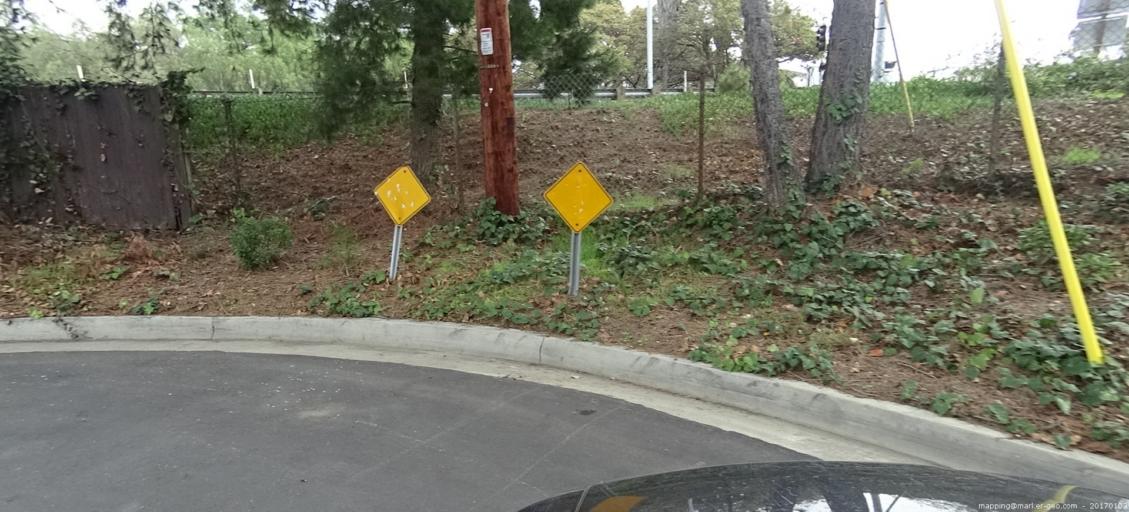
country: US
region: California
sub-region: Orange County
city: Dana Point
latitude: 33.4584
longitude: -117.6570
